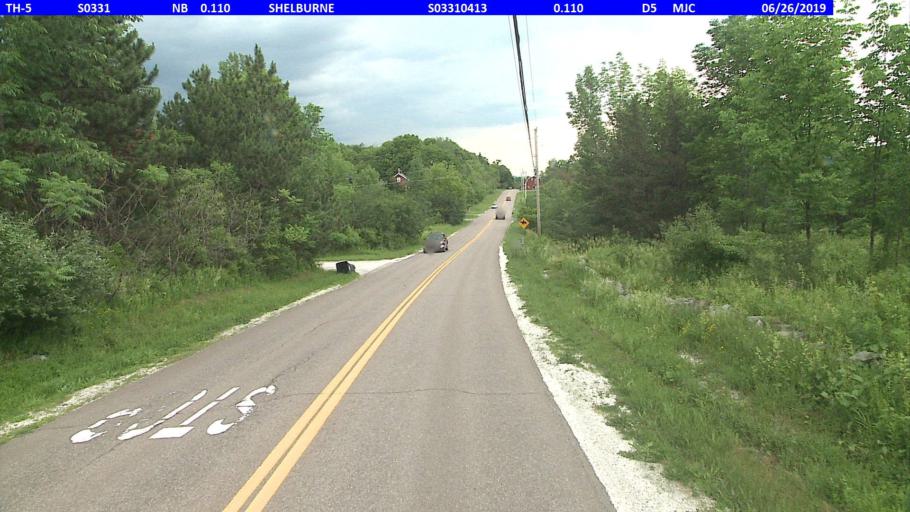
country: US
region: Vermont
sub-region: Chittenden County
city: Hinesburg
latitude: 44.3732
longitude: -73.1810
